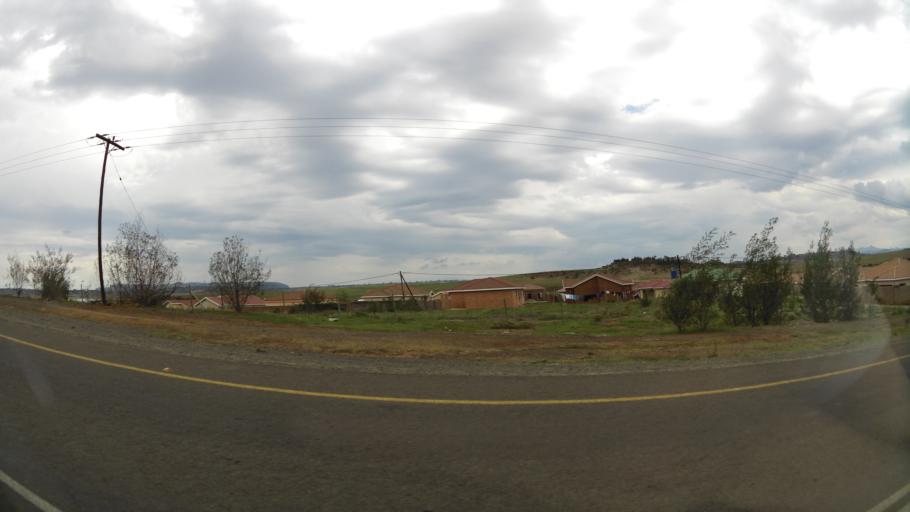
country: LS
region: Maseru
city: Maseru
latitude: -29.3946
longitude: 27.4749
